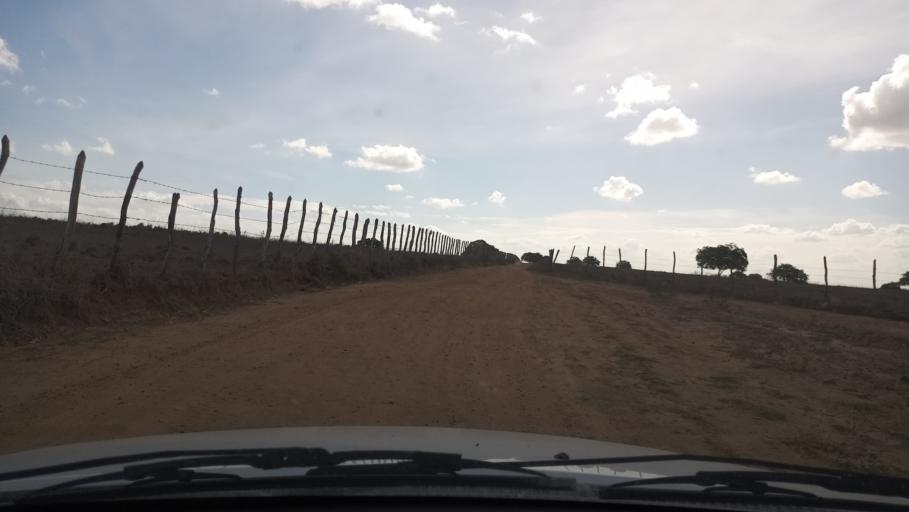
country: BR
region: Rio Grande do Norte
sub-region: Goianinha
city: Goianinha
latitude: -6.3037
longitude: -35.3020
